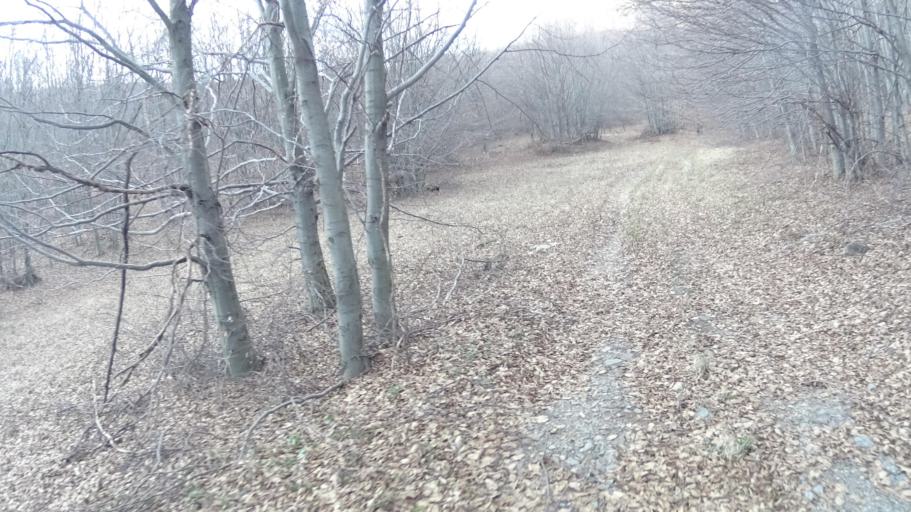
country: HU
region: Heves
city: Szilvasvarad
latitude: 48.0856
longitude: 20.4823
